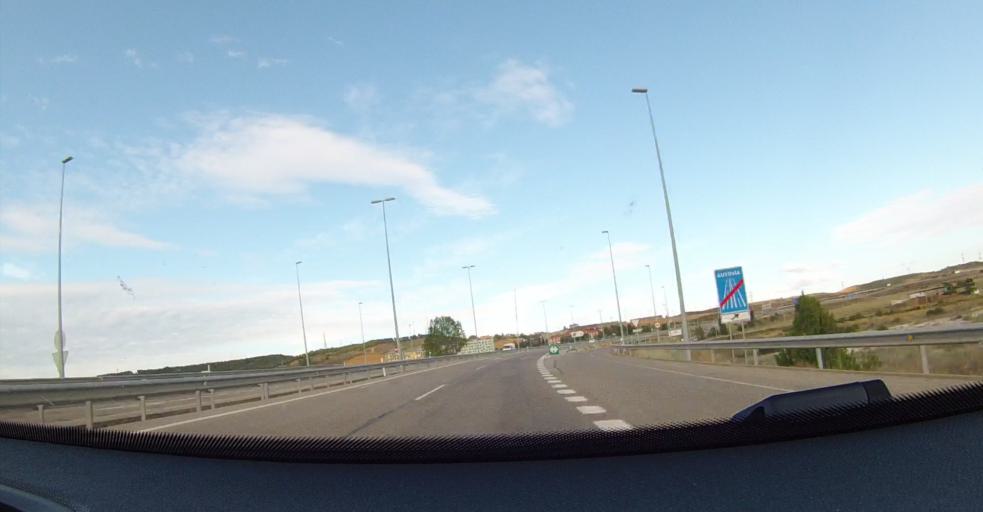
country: ES
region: Castille and Leon
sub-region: Provincia de Leon
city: Leon
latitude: 42.5753
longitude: -5.5561
